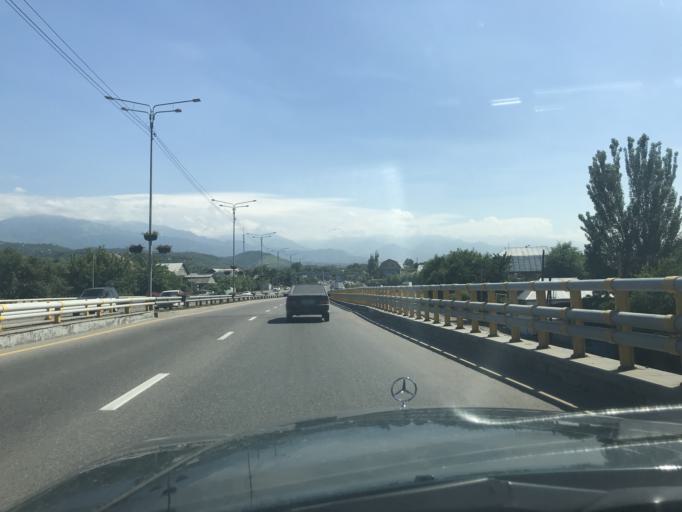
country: KZ
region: Almaty Qalasy
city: Almaty
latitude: 43.2831
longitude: 76.9866
